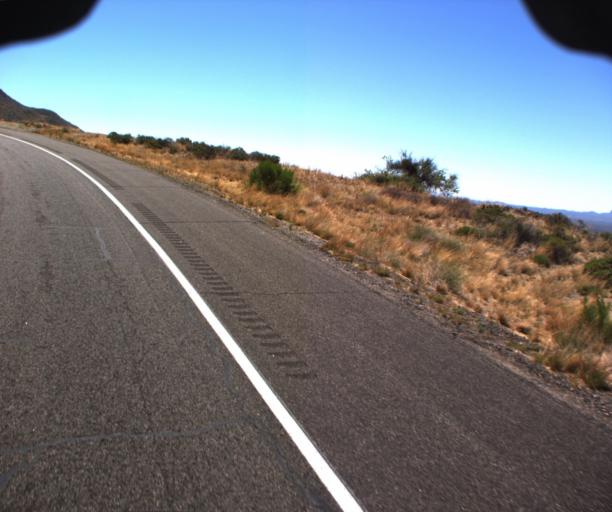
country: US
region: Arizona
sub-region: Yavapai County
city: Congress
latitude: 34.2010
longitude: -112.7814
